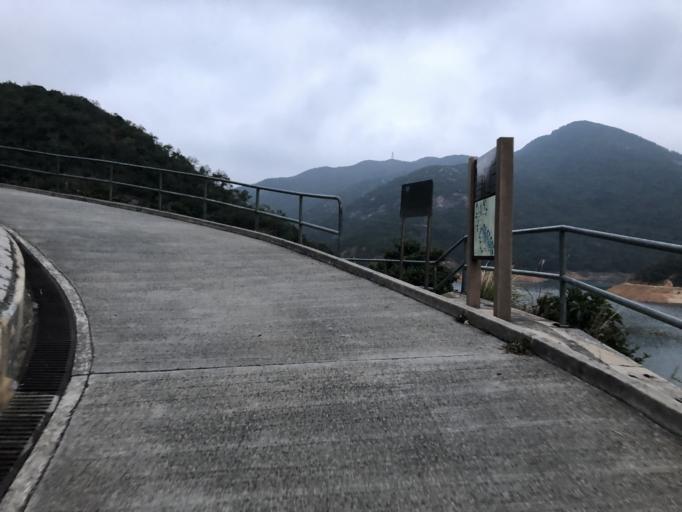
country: HK
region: Wanchai
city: Wan Chai
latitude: 22.2570
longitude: 114.2101
